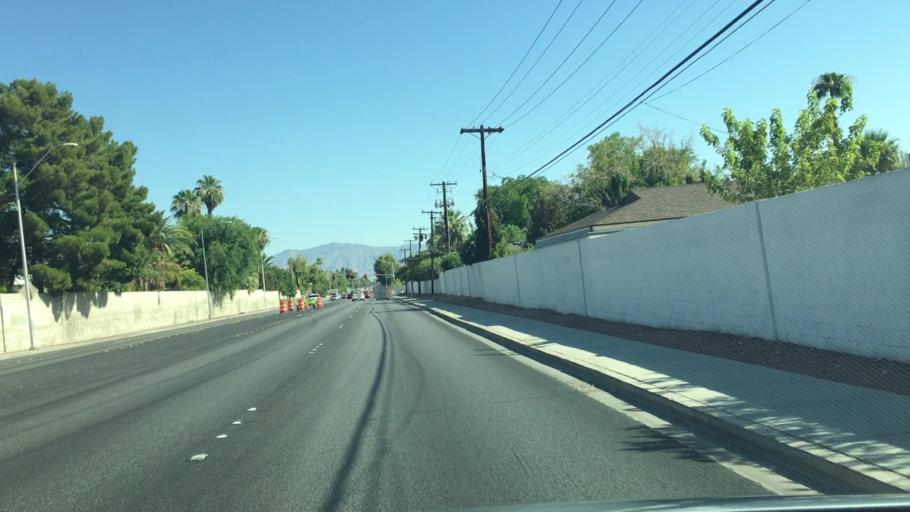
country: US
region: Nevada
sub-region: Clark County
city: Las Vegas
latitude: 36.1493
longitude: -115.1730
